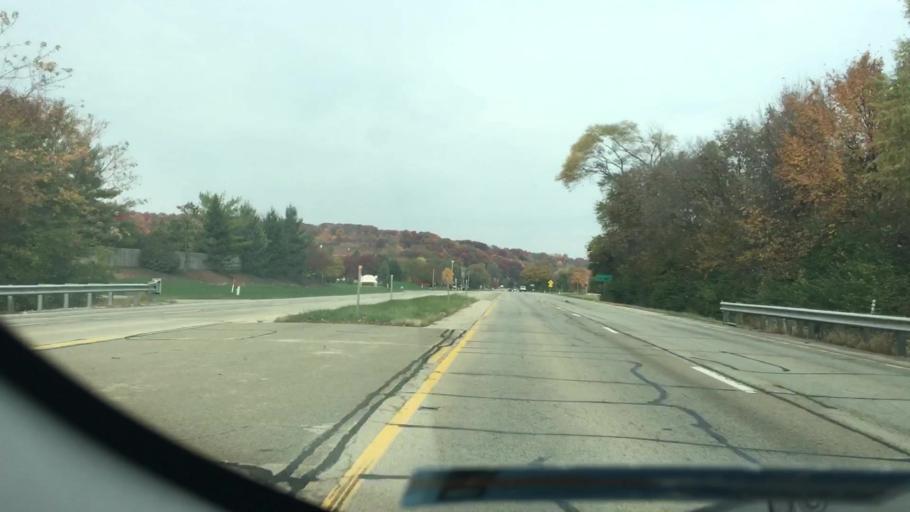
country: US
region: Illinois
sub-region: Peoria County
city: Peoria Heights
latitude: 40.7691
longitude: -89.5717
